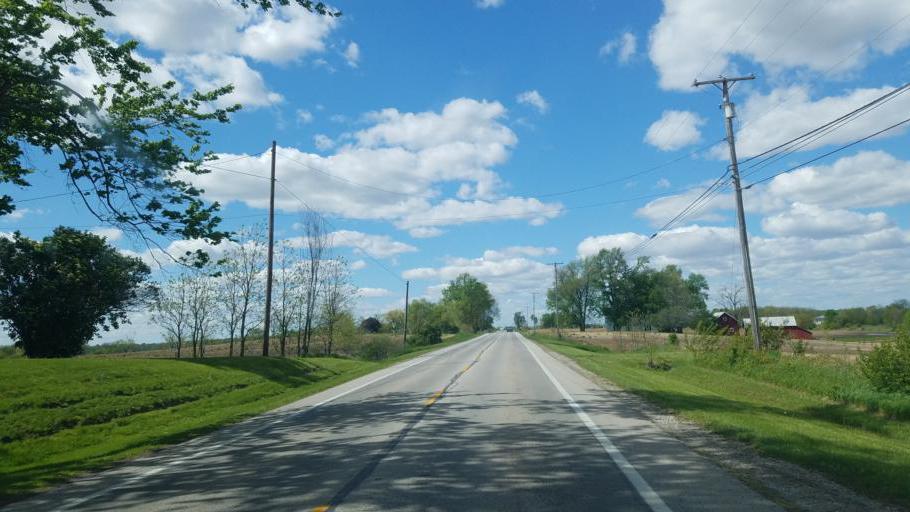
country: US
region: Ohio
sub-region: Marion County
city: Marion
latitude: 40.4919
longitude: -83.0894
